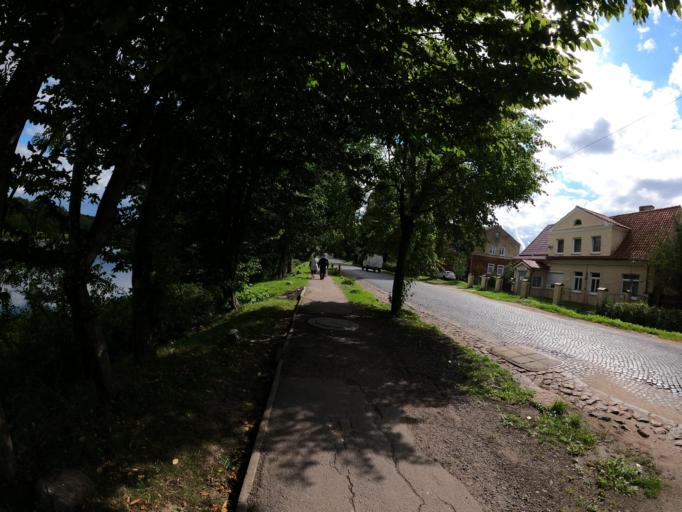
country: RU
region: Kaliningrad
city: Zheleznodorozhnyy
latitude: 54.3570
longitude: 21.3070
